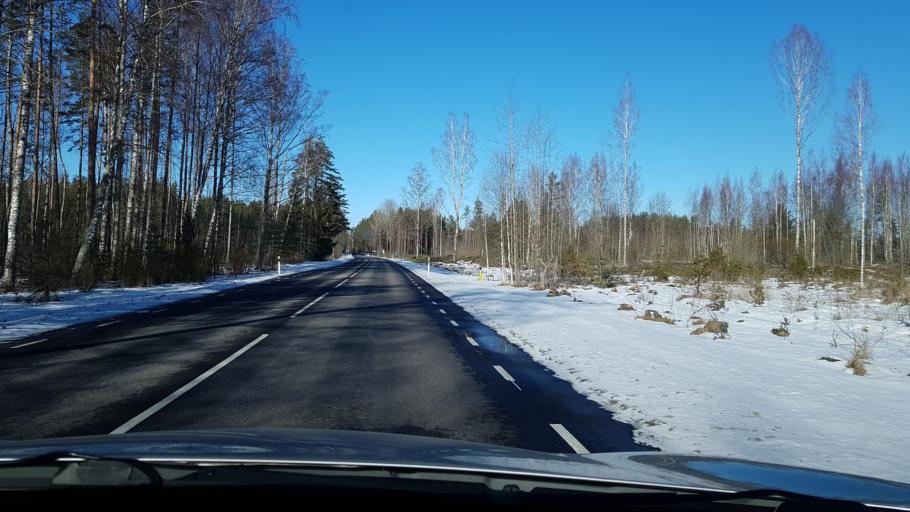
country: EE
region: Polvamaa
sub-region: Raepina vald
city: Rapina
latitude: 57.9859
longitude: 27.5653
